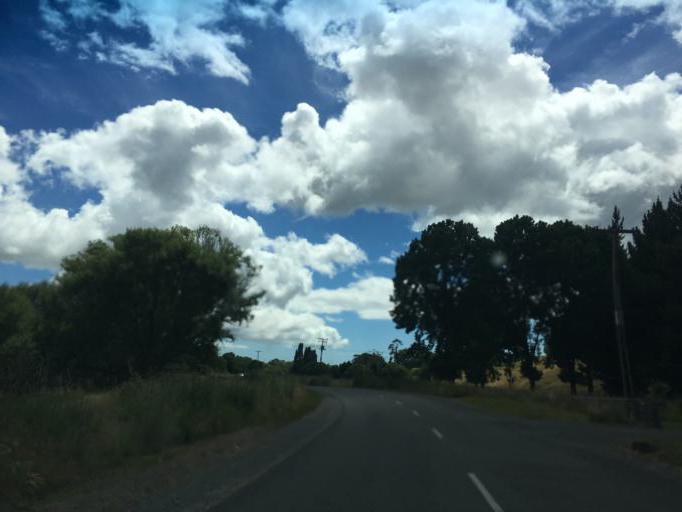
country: NZ
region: Hawke's Bay
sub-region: Hastings District
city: Hastings
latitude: -39.7520
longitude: 176.8744
